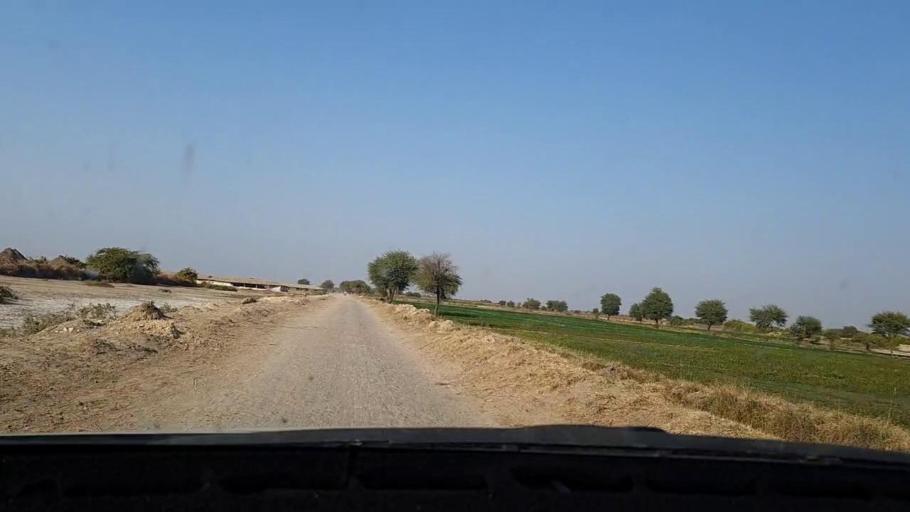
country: PK
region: Sindh
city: Tando Mittha Khan
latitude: 25.8412
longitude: 69.3326
